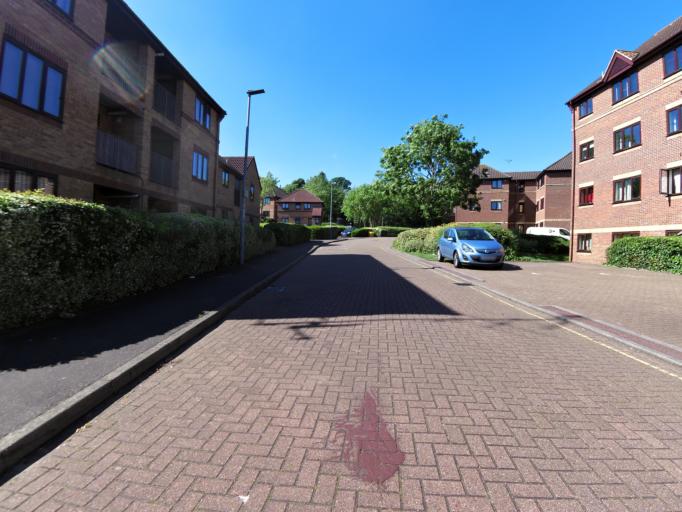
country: GB
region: England
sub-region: Norfolk
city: Thorpe Hamlet
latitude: 52.6238
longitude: 1.3191
